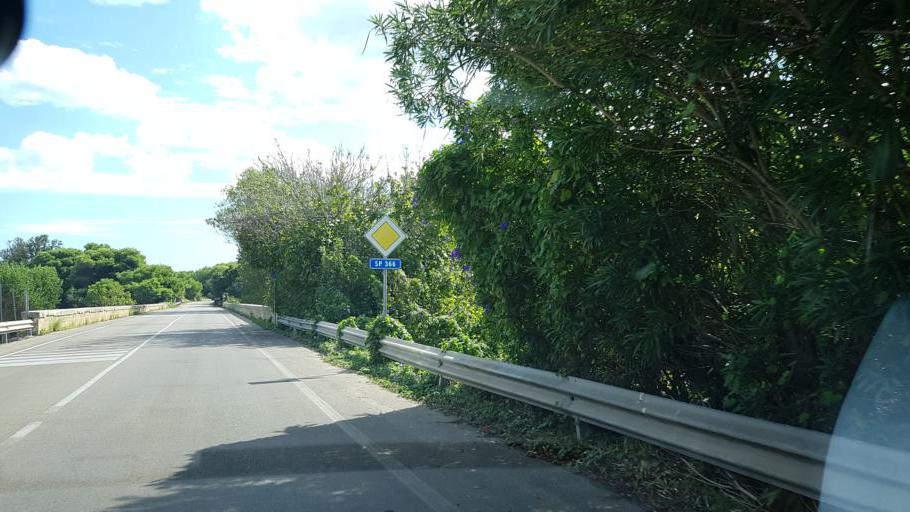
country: IT
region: Apulia
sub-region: Provincia di Lecce
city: Borgagne
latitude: 40.2701
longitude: 18.4296
